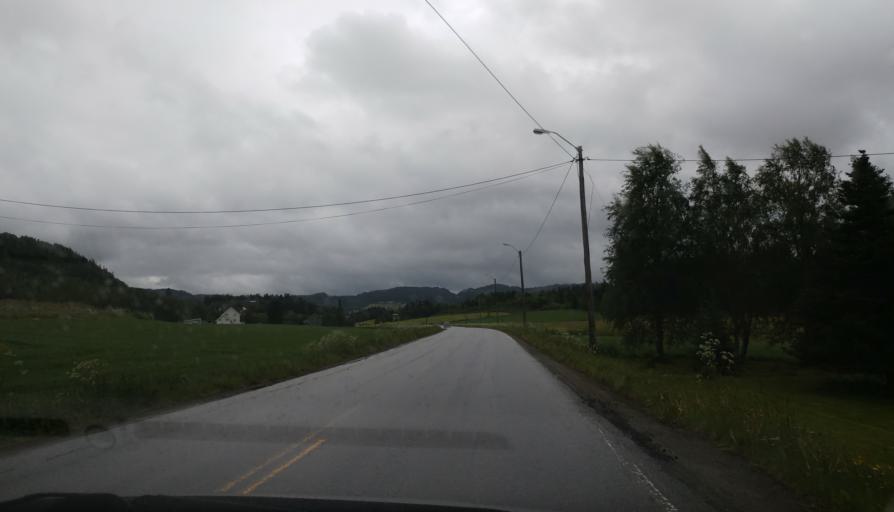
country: NO
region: Sor-Trondelag
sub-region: Selbu
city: Mebonden
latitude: 63.2671
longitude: 11.0793
